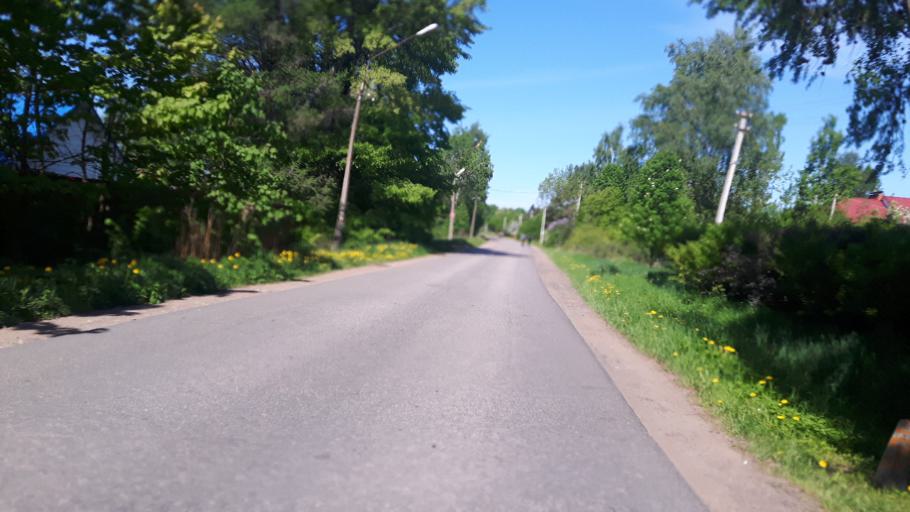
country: RU
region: Leningrad
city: Lebyazh'ye
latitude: 59.9664
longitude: 29.4011
